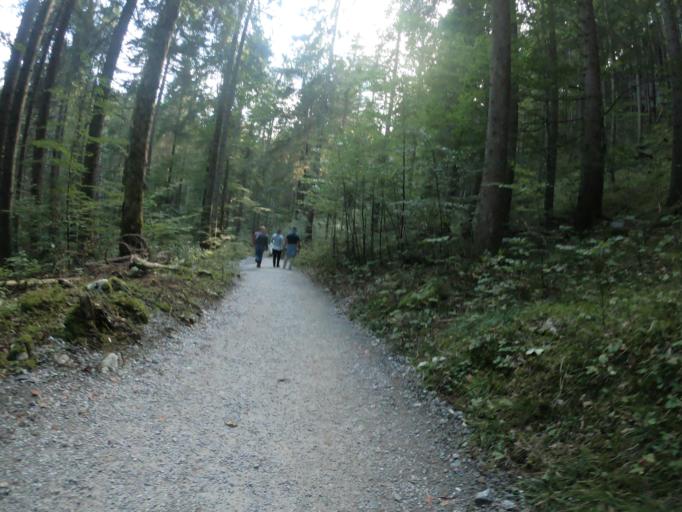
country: AT
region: Tyrol
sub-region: Politischer Bezirk Reutte
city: Ehenbichl
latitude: 47.4614
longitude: 10.7132
